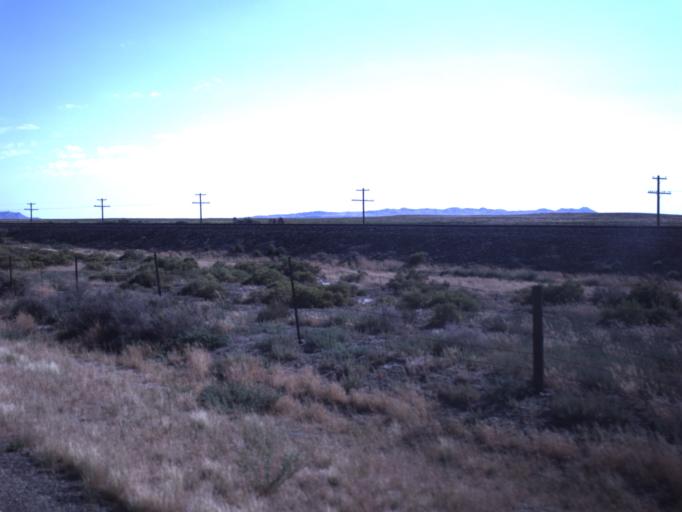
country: US
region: Utah
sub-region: Beaver County
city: Milford
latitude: 38.6324
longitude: -112.9840
